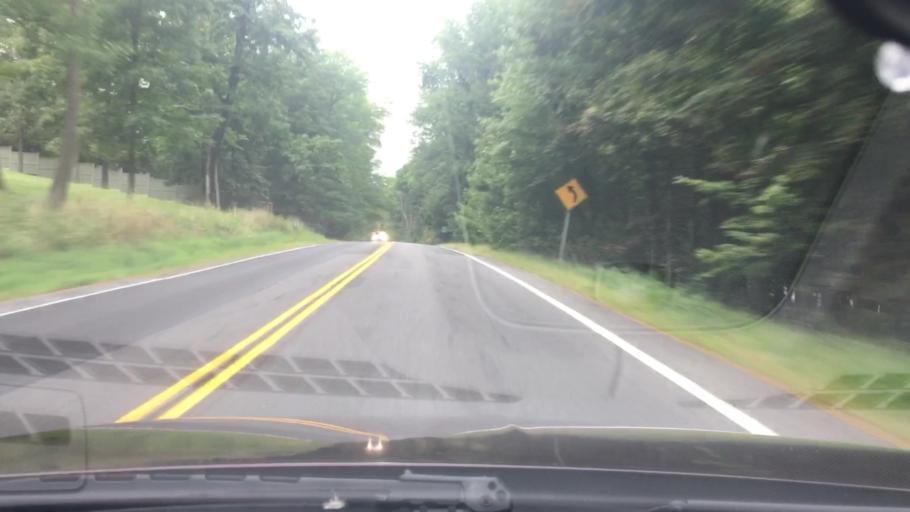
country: US
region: New York
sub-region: Dutchess County
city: Millbrook
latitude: 41.7931
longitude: -73.6895
